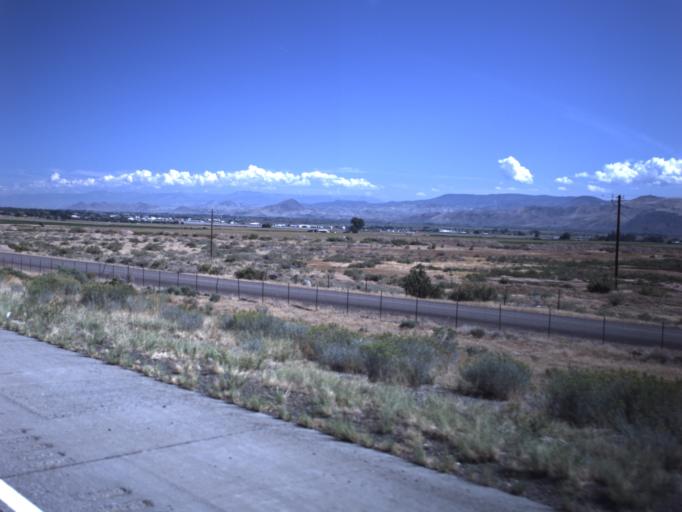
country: US
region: Utah
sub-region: Sevier County
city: Richfield
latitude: 38.7172
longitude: -112.1337
